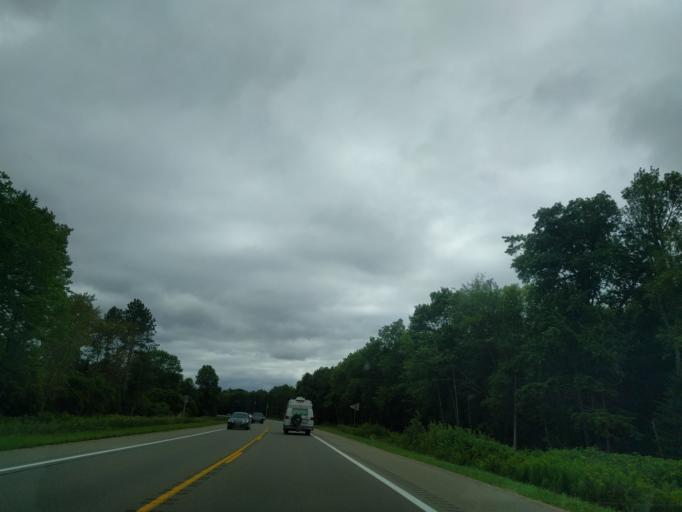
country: US
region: Michigan
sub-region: Menominee County
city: Menominee
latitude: 45.3070
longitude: -87.4391
